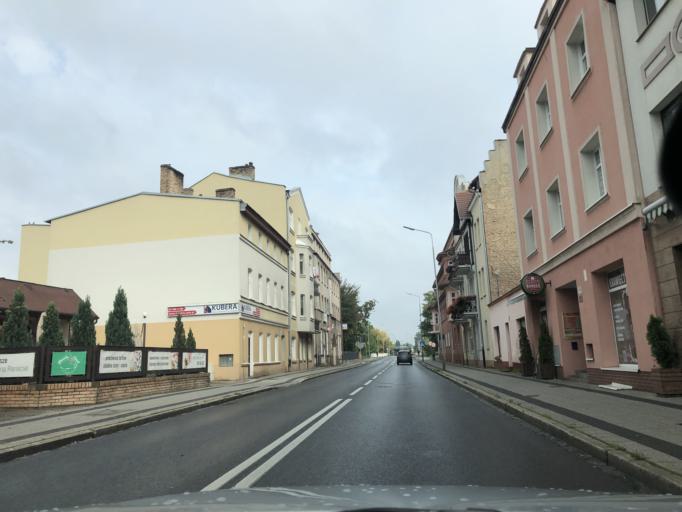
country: PL
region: Greater Poland Voivodeship
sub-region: Powiat pilski
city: Pila
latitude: 53.1491
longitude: 16.7419
